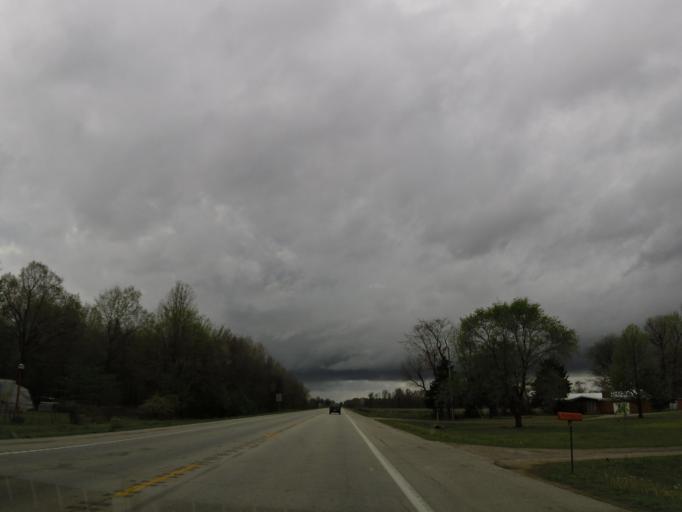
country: US
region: Arkansas
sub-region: Clay County
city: Corning
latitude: 36.5441
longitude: -90.5242
